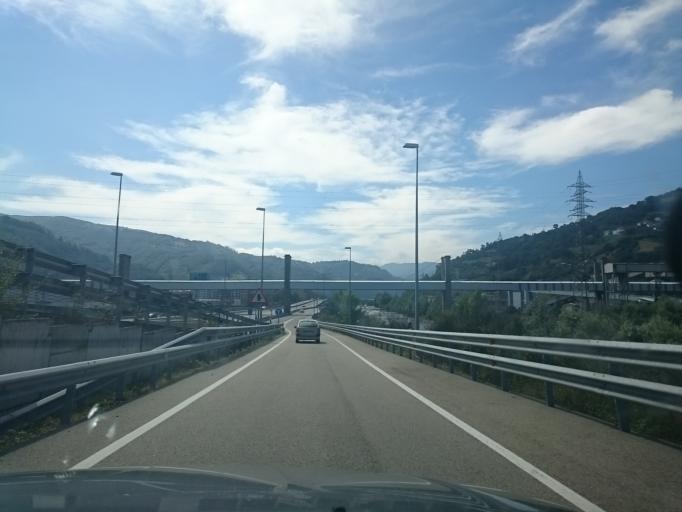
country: ES
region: Asturias
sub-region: Province of Asturias
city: Mieres
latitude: 43.2603
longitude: -5.7835
